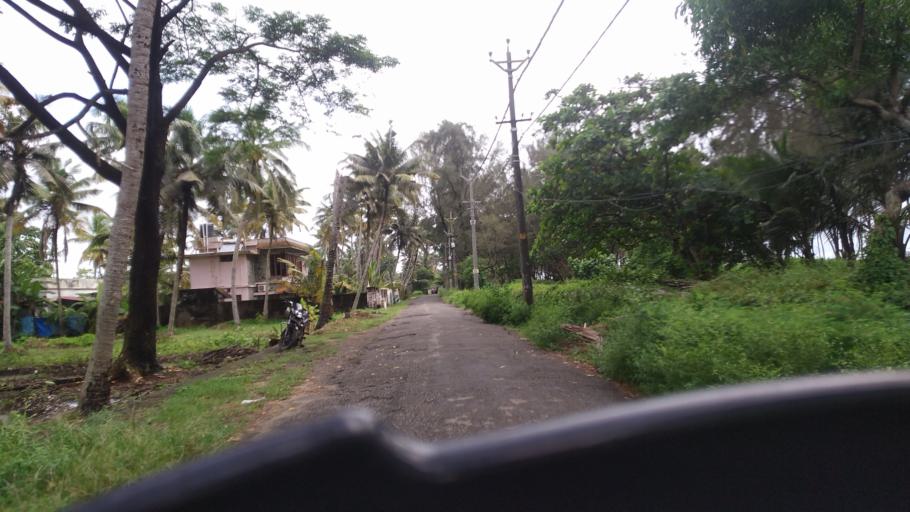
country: IN
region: Kerala
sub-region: Ernakulam
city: Elur
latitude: 10.1126
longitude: 76.1871
